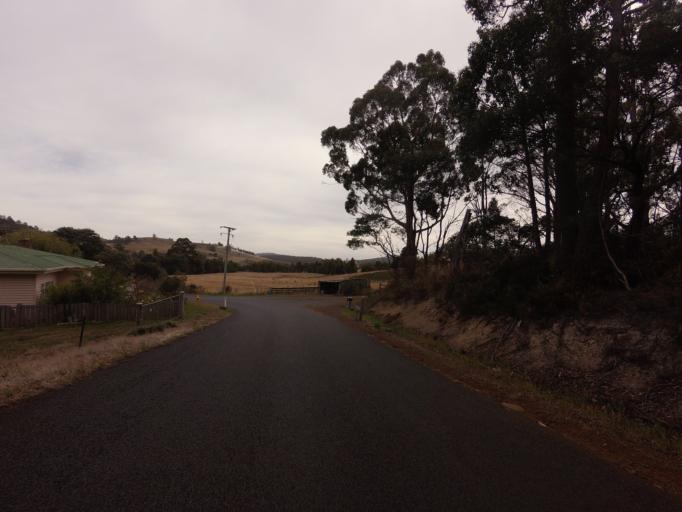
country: AU
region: Tasmania
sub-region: Sorell
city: Sorell
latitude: -42.4932
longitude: 147.5682
